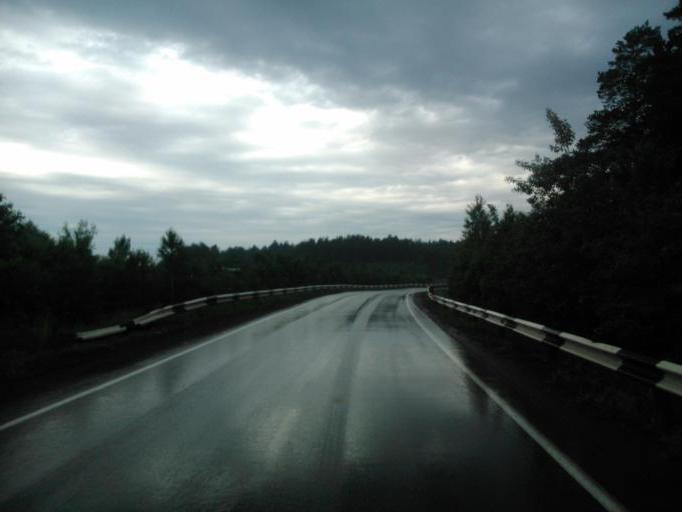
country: RU
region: Sverdlovsk
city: Istok
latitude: 56.8047
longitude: 60.7922
